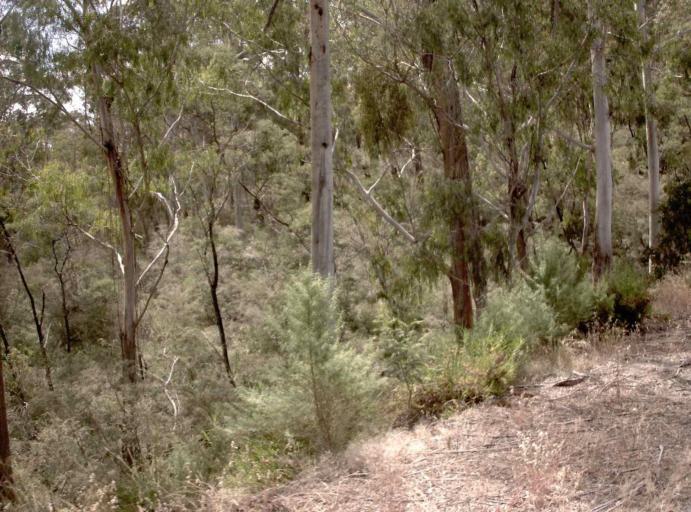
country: AU
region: New South Wales
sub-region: Bega Valley
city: Eden
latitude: -37.4648
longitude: 149.5874
